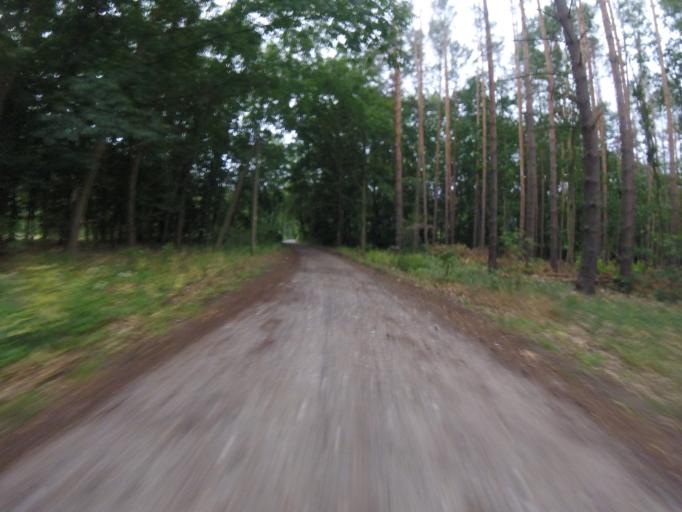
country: DE
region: Brandenburg
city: Bestensee
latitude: 52.2288
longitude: 13.7185
